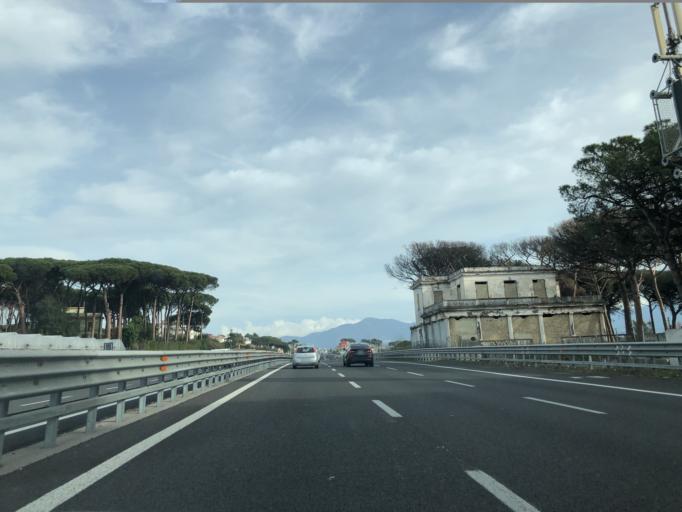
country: IT
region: Campania
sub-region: Provincia di Napoli
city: Torre del Greco
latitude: 40.7755
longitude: 14.4043
